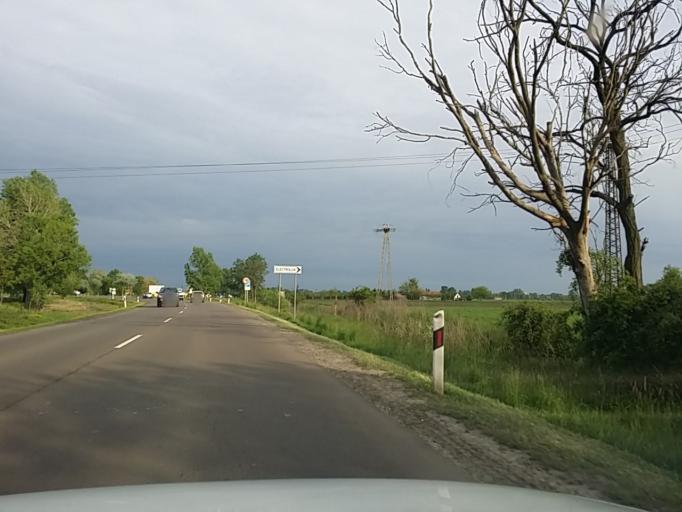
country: HU
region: Jasz-Nagykun-Szolnok
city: Jaszbereny
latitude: 47.5170
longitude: 19.8778
